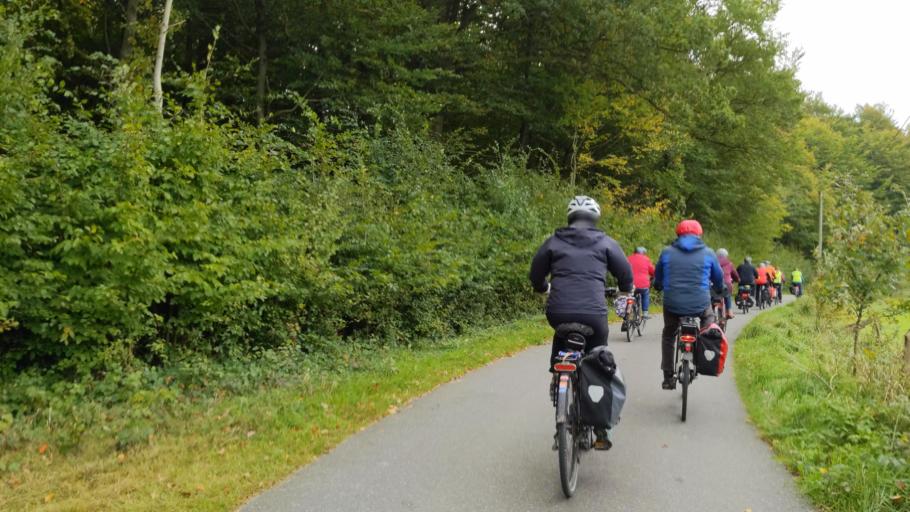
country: DE
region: Schleswig-Holstein
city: Rehhorst
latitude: 53.8615
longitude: 10.4741
